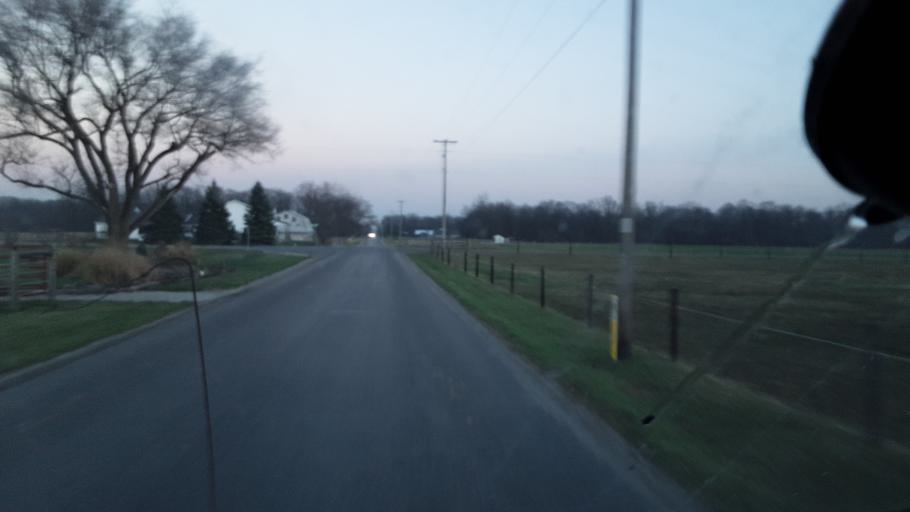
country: US
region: Indiana
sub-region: Allen County
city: Harlan
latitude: 41.2397
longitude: -84.9245
